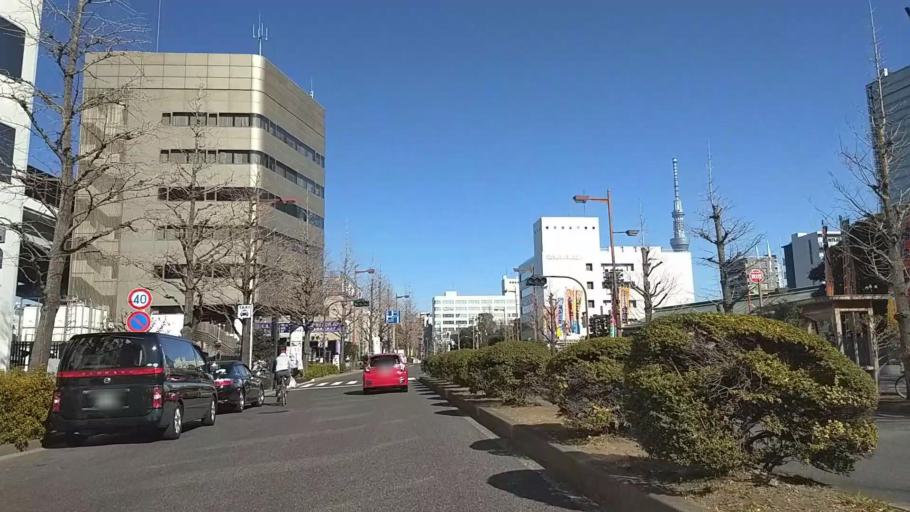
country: JP
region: Tokyo
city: Urayasu
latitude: 35.6969
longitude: 139.7920
